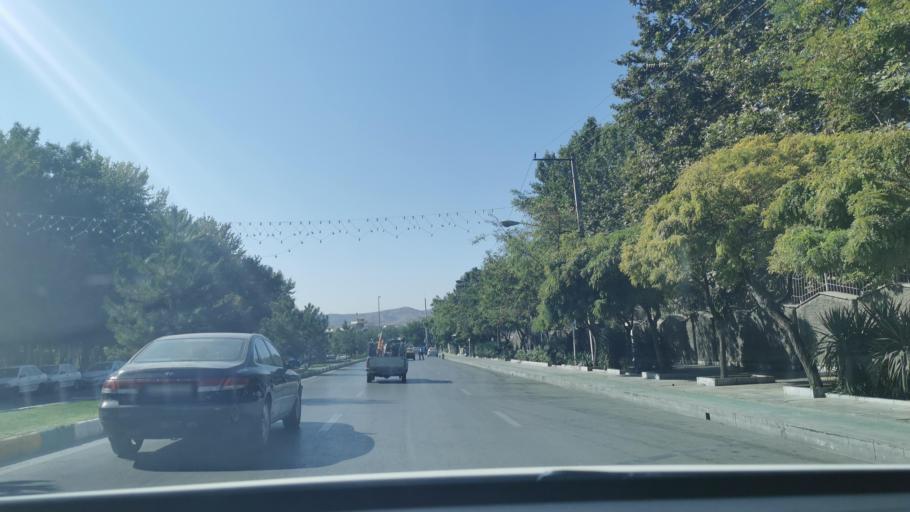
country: IR
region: Razavi Khorasan
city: Mashhad
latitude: 36.3198
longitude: 59.5327
